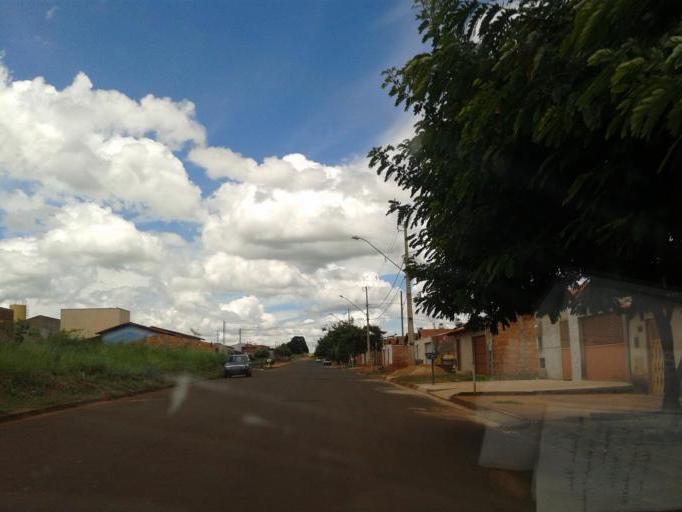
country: BR
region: Minas Gerais
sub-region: Santa Vitoria
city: Santa Vitoria
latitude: -18.8476
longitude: -50.1341
